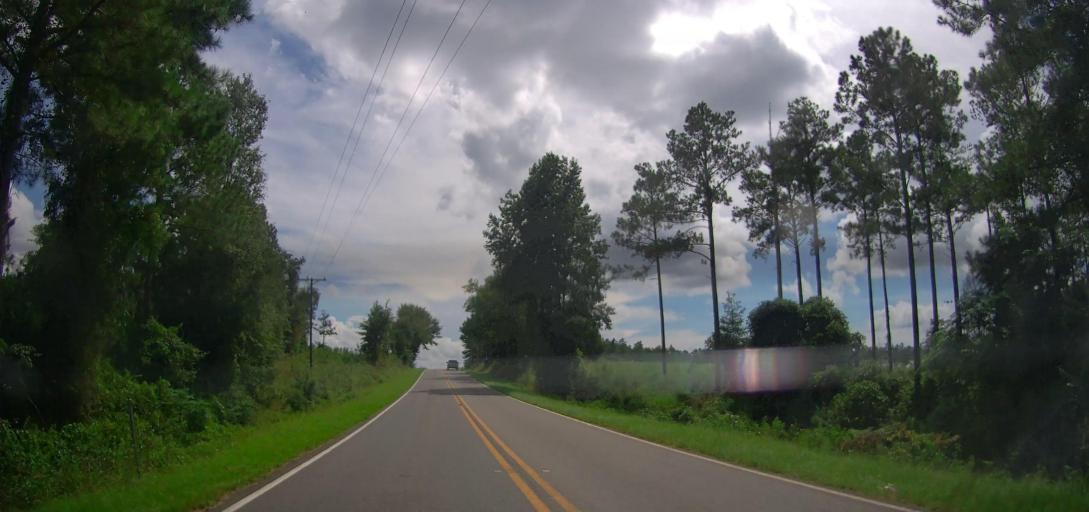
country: US
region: Georgia
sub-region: Taylor County
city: Butler
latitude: 32.4490
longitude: -84.1958
